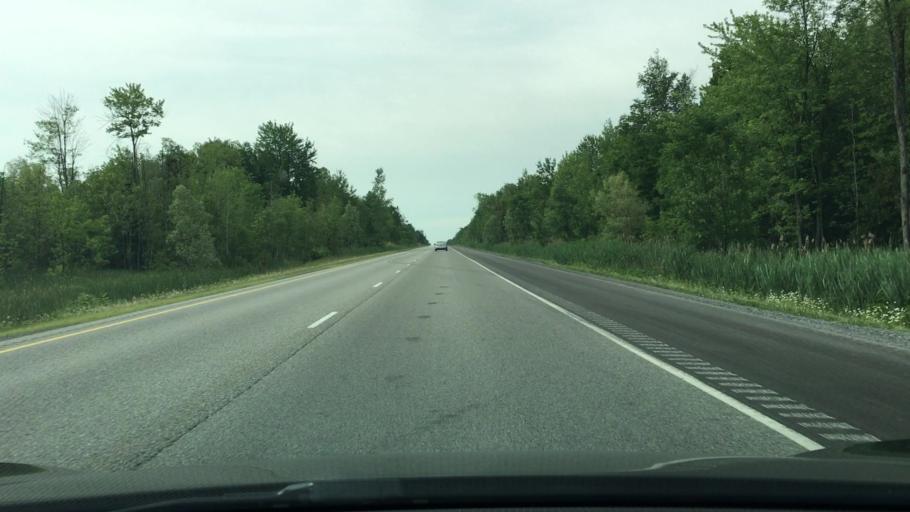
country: CA
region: Ontario
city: Prescott
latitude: 44.9280
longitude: -75.5754
